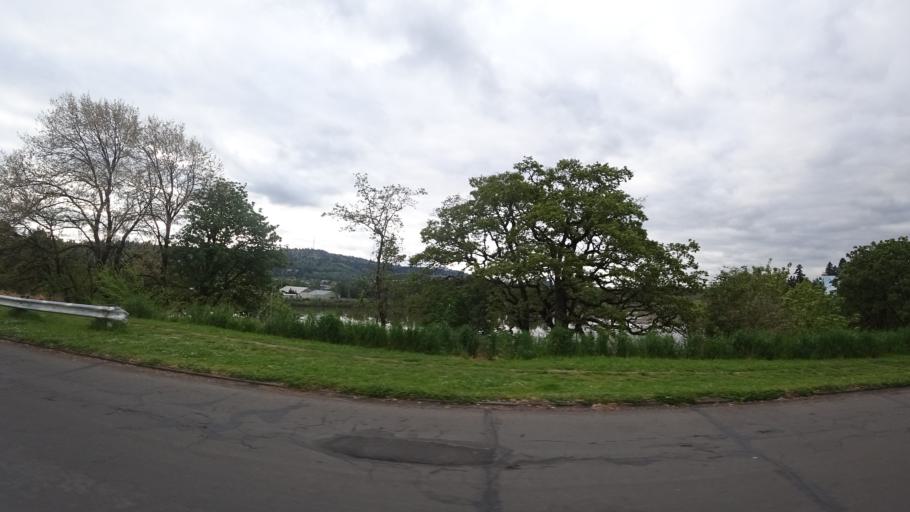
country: US
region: Oregon
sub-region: Clackamas County
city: Milwaukie
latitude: 45.4708
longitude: -122.6548
